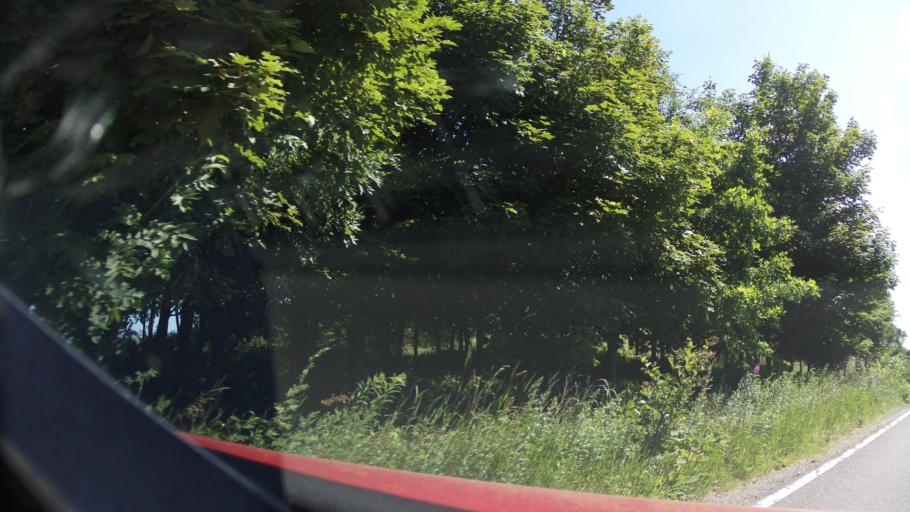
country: GB
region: England
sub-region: Derbyshire
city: Ashbourne
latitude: 53.0707
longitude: -1.7496
